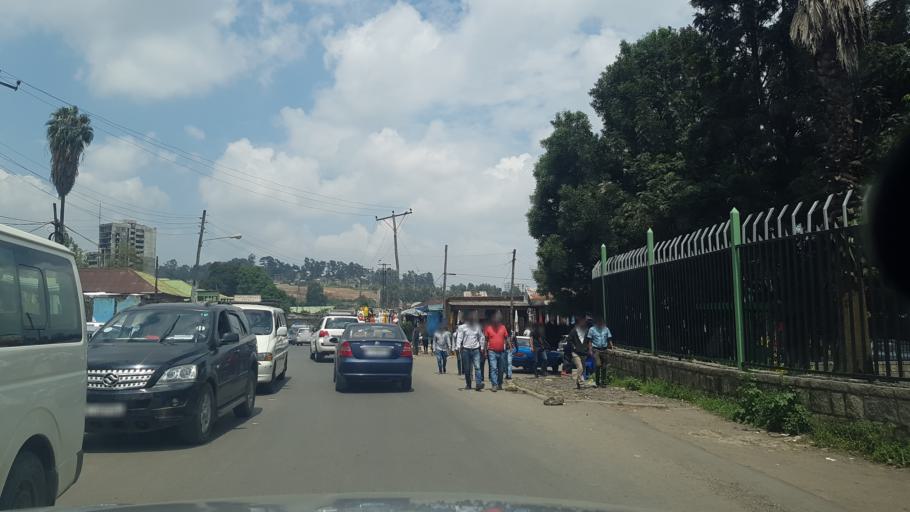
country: ET
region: Adis Abeba
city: Addis Ababa
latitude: 9.0214
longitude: 38.7533
